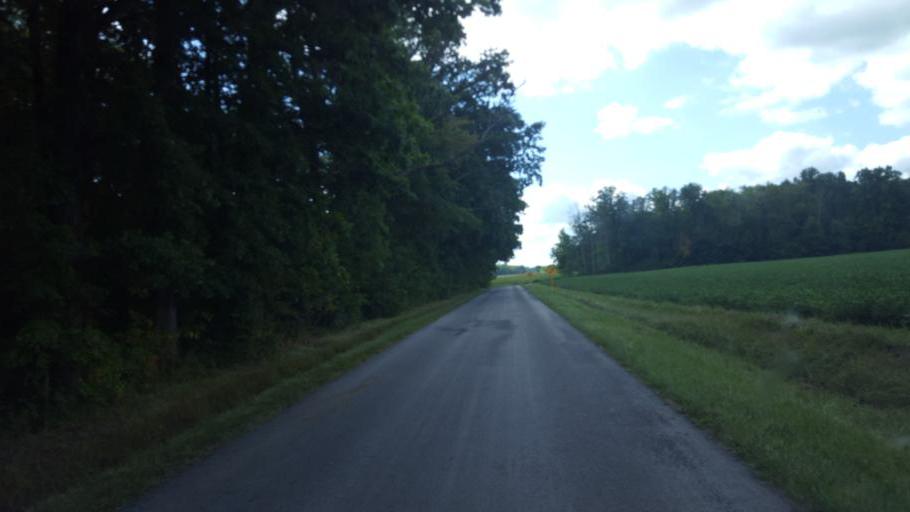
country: US
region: Ohio
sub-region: Medina County
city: Lodi
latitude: 41.0649
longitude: -82.0953
